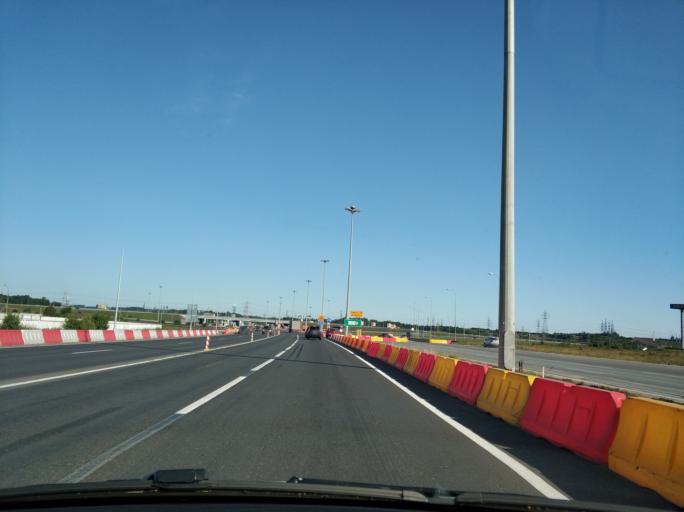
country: RU
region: Leningrad
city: Bugry
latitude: 60.0881
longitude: 30.3746
